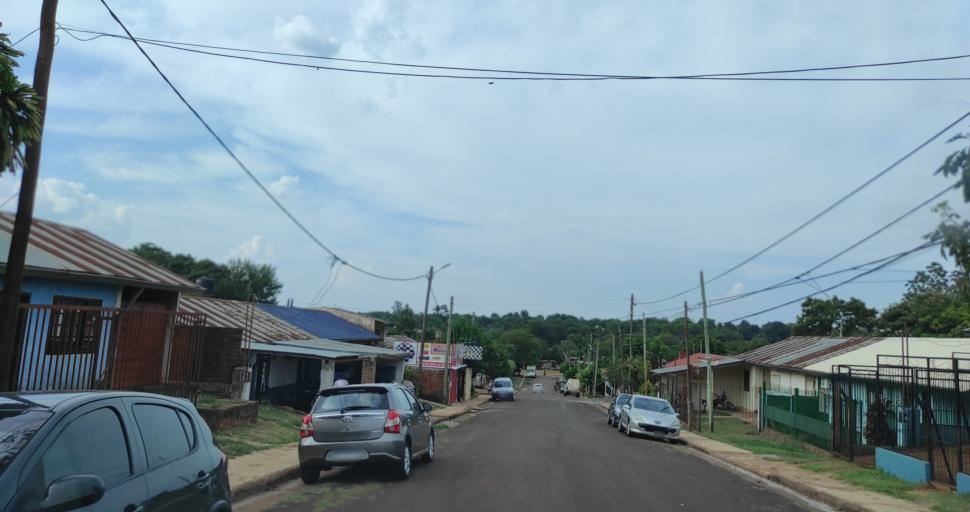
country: AR
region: Misiones
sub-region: Departamento de Capital
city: Posadas
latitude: -27.3958
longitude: -55.9373
